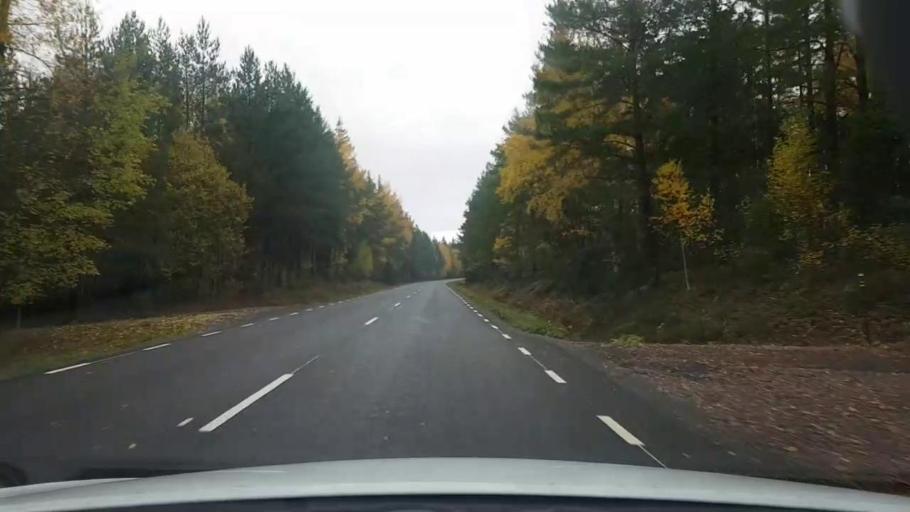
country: SE
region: OErebro
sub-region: Laxa Kommun
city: Laxa
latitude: 58.7996
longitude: 14.5424
